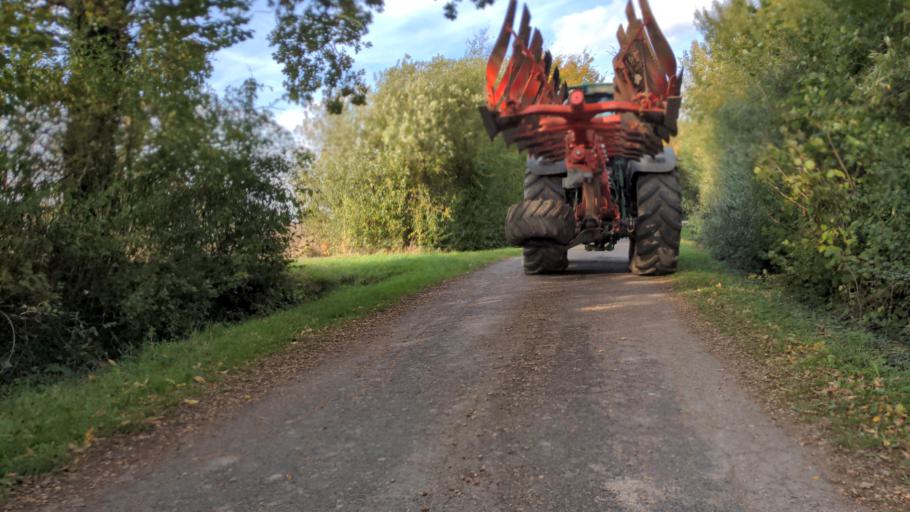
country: DE
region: Schleswig-Holstein
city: Monkhagen
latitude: 53.9450
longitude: 10.5635
